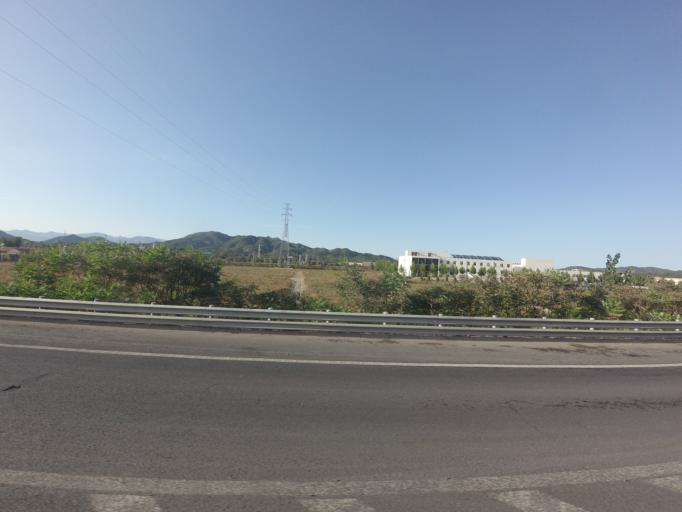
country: CN
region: Beijing
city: Jugezhuang
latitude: 40.3947
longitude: 116.9259
